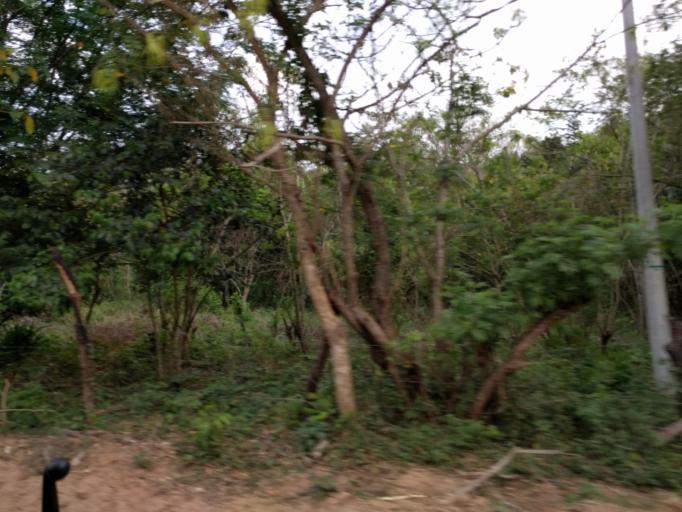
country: BO
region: Santa Cruz
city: Santa Rita
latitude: -17.9326
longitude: -63.3791
